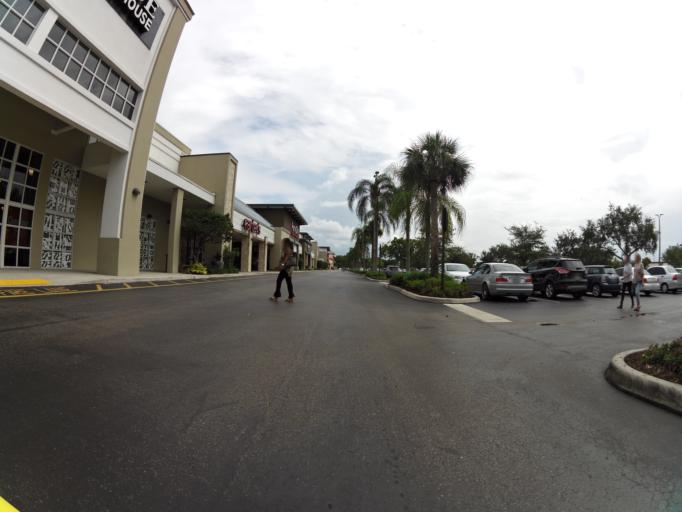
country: US
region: Florida
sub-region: Broward County
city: Pine Island Ridge
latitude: 26.0936
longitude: -80.2477
